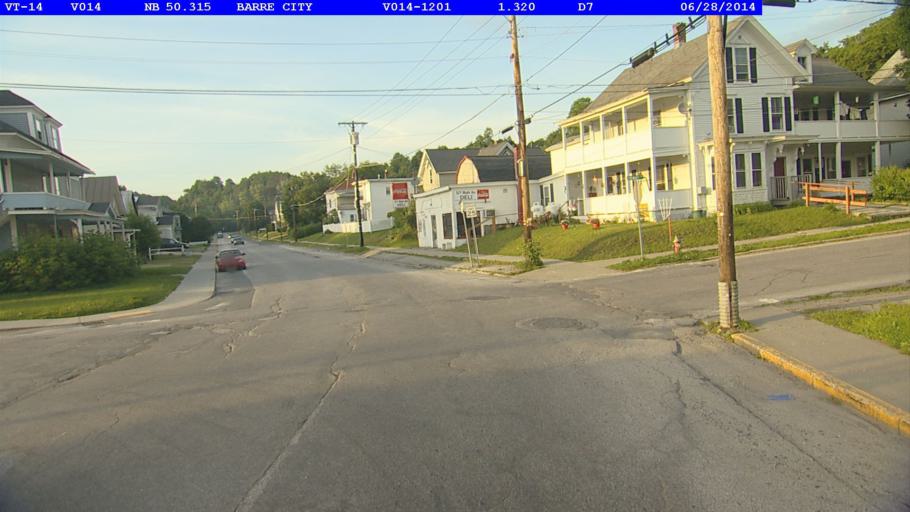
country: US
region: Vermont
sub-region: Washington County
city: Barre
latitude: 44.2039
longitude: -72.5057
